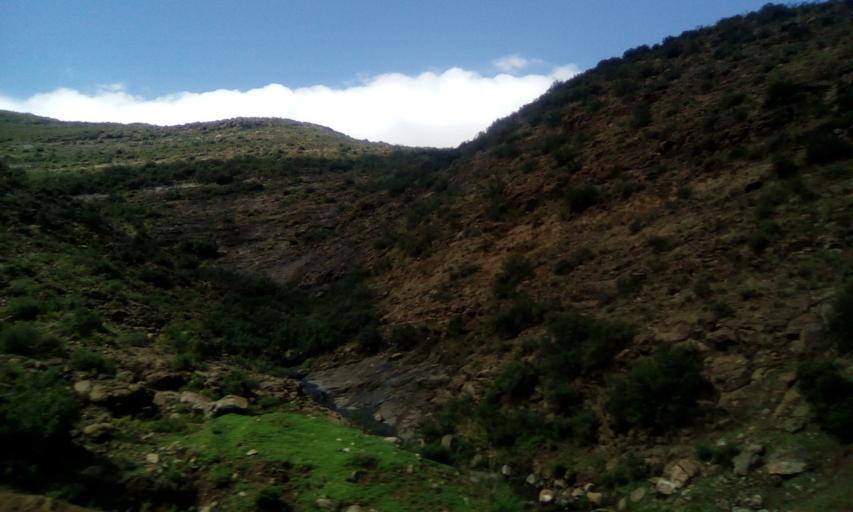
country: LS
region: Maseru
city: Nako
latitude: -29.6565
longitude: 27.8390
